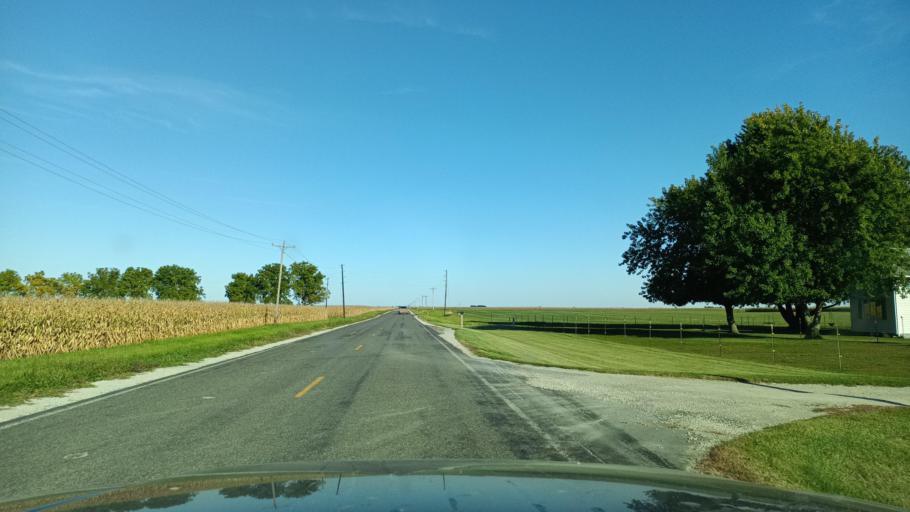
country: US
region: Illinois
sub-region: McLean County
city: Le Roy
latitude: 40.2244
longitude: -88.8016
